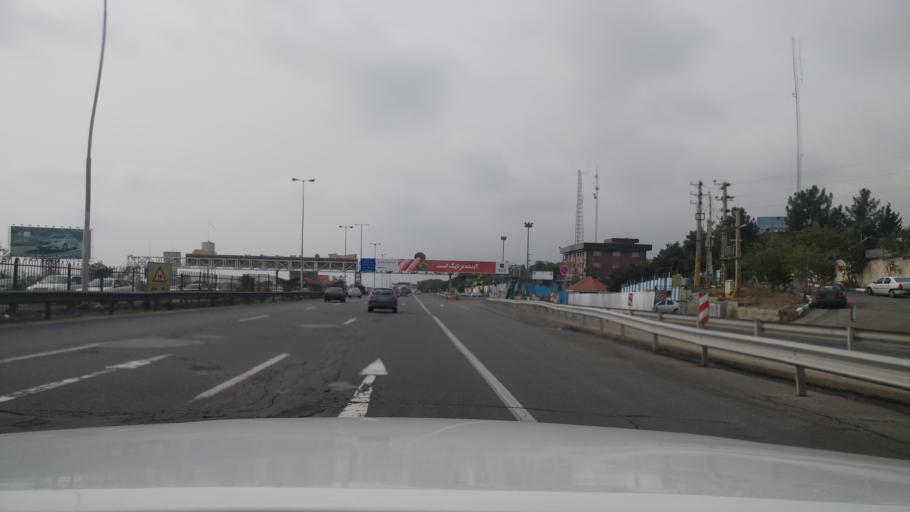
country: IR
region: Tehran
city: Shahr-e Qods
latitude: 35.7163
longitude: 51.2402
